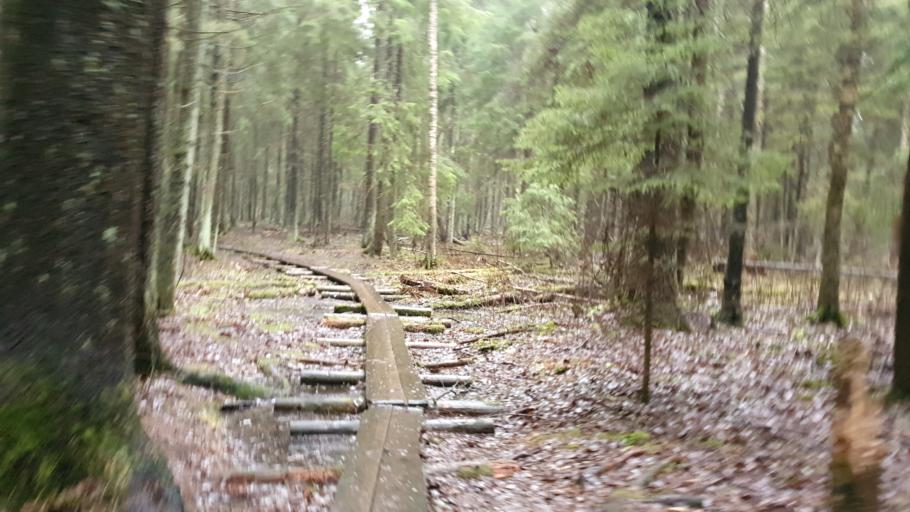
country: FI
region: Uusimaa
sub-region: Helsinki
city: Helsinki
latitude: 60.2703
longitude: 24.9301
